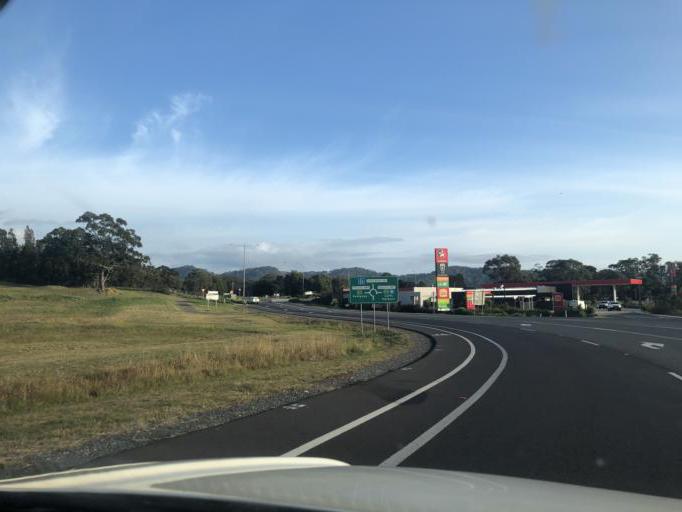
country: AU
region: New South Wales
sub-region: Coffs Harbour
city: Boambee
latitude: -30.3221
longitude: 153.0876
